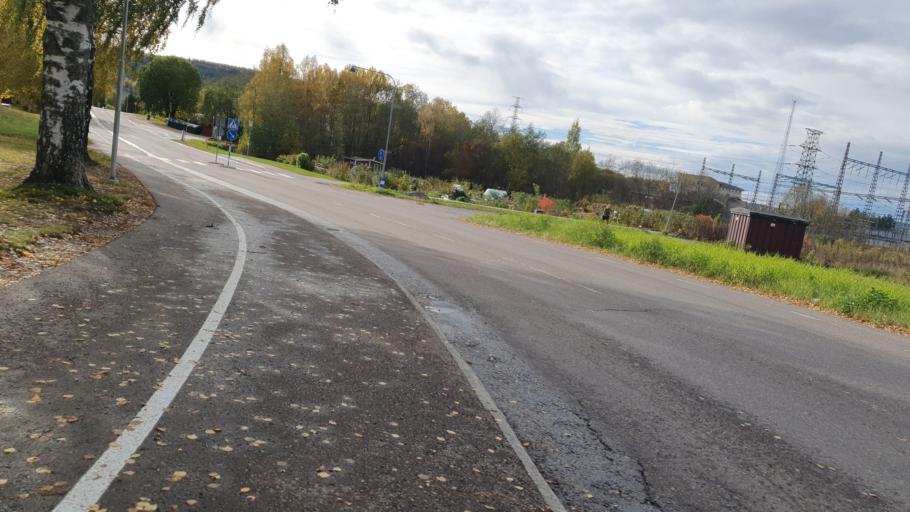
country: SE
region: Vaesternorrland
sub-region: Sundsvalls Kommun
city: Sundsvall
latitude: 62.4069
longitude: 17.2458
